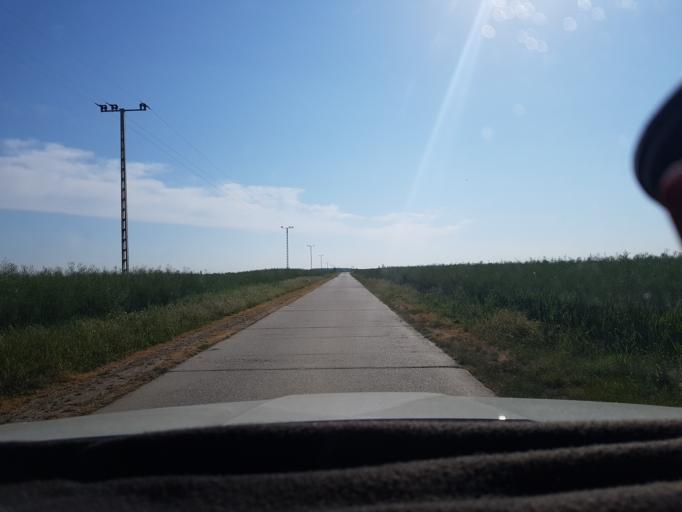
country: HU
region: Tolna
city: Decs
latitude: 46.2743
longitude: 18.7267
